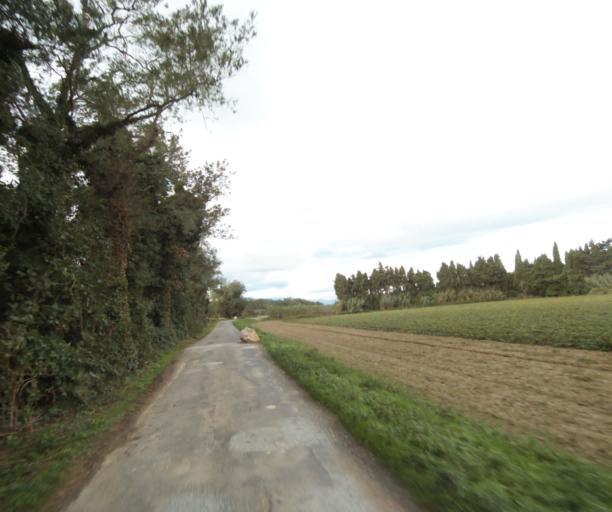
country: FR
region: Languedoc-Roussillon
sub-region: Departement des Pyrenees-Orientales
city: Latour-Bas-Elne
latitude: 42.5840
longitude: 3.0197
